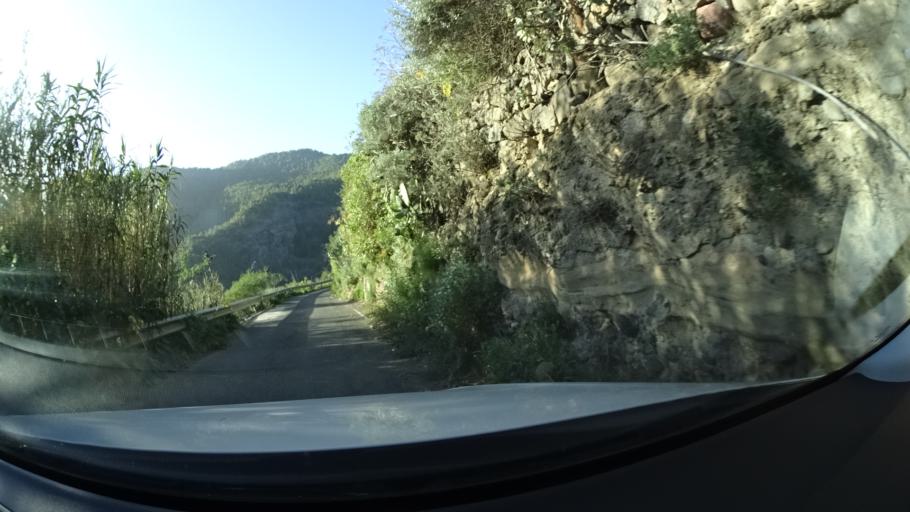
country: ES
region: Canary Islands
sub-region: Provincia de Las Palmas
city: Artenara
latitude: 28.0475
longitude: -15.6656
